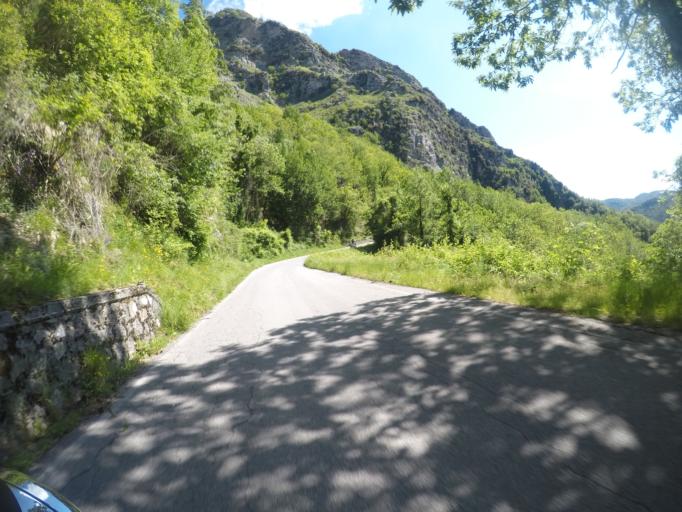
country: IT
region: Tuscany
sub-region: Provincia di Lucca
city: Careggine
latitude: 44.0720
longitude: 10.3187
